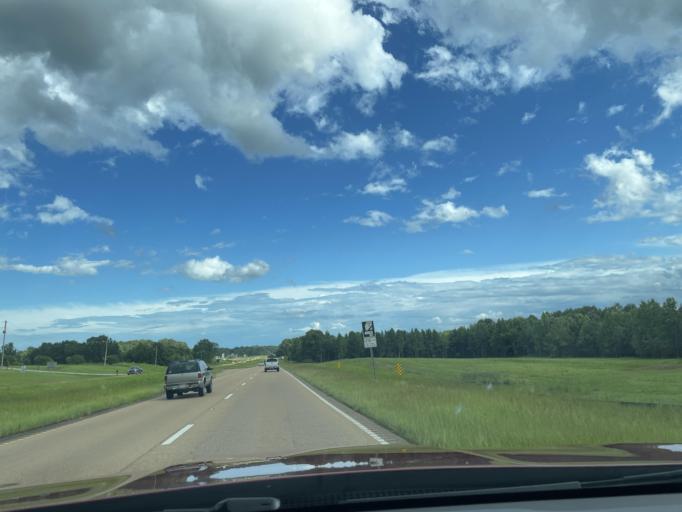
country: US
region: Mississippi
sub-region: Madison County
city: Flora
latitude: 32.5354
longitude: -90.3177
